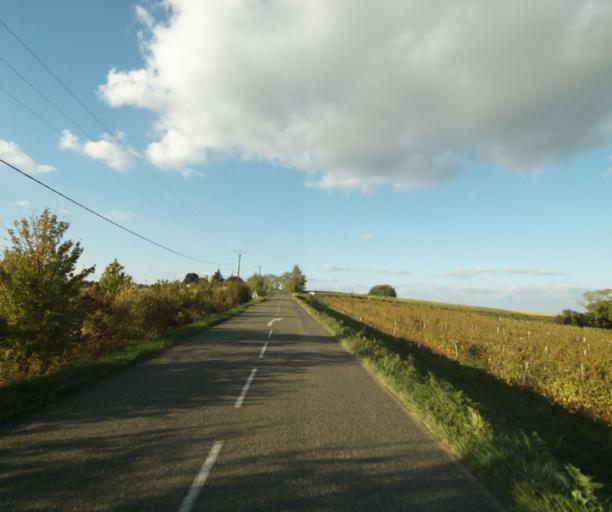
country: FR
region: Midi-Pyrenees
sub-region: Departement du Gers
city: Eauze
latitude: 43.7447
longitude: 0.1361
